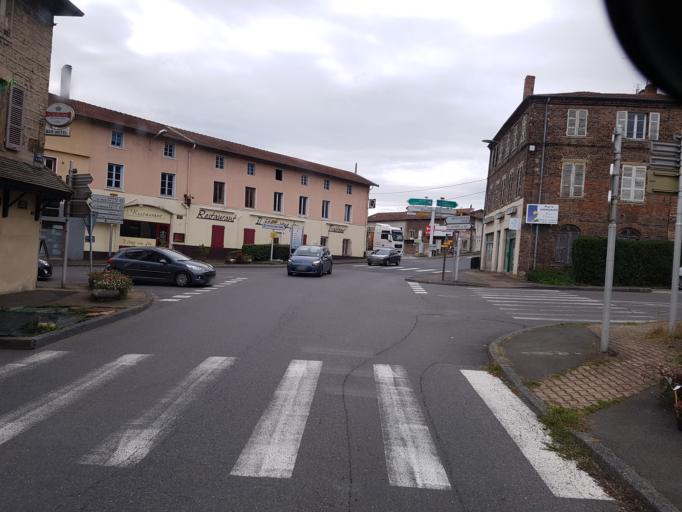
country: FR
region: Rhone-Alpes
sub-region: Departement du Rhone
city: Sainte-Foy-l'Argentiere
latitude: 45.7101
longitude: 4.4673
